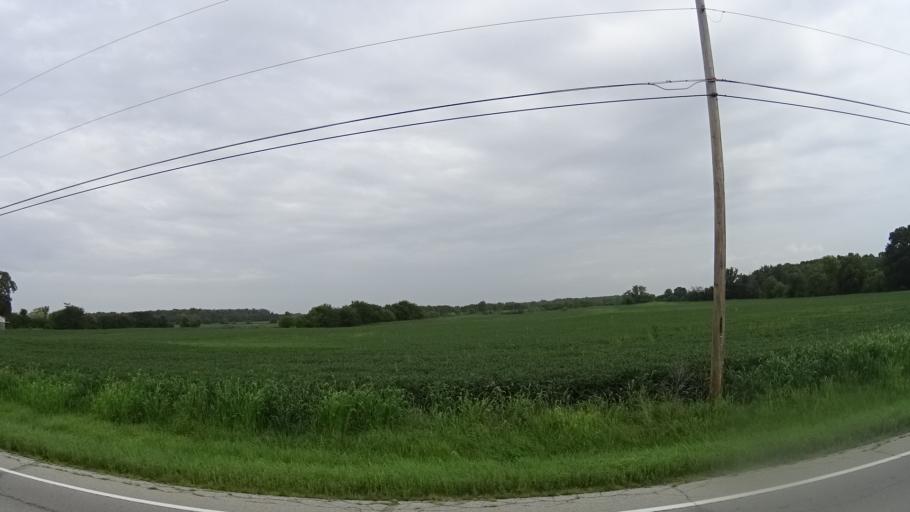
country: US
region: Indiana
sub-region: Madison County
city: Edgewood
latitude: 40.1013
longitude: -85.7929
